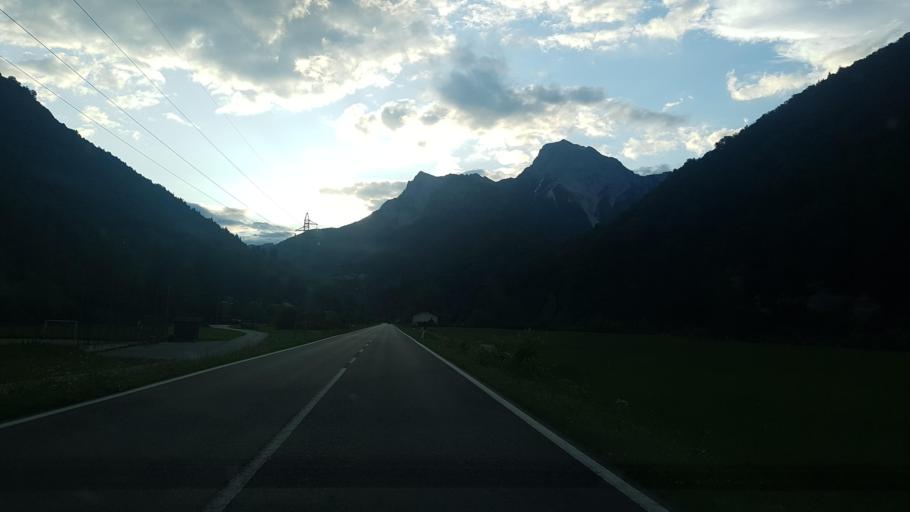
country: IT
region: Friuli Venezia Giulia
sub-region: Provincia di Udine
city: Zuglio
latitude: 46.4678
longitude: 13.0584
